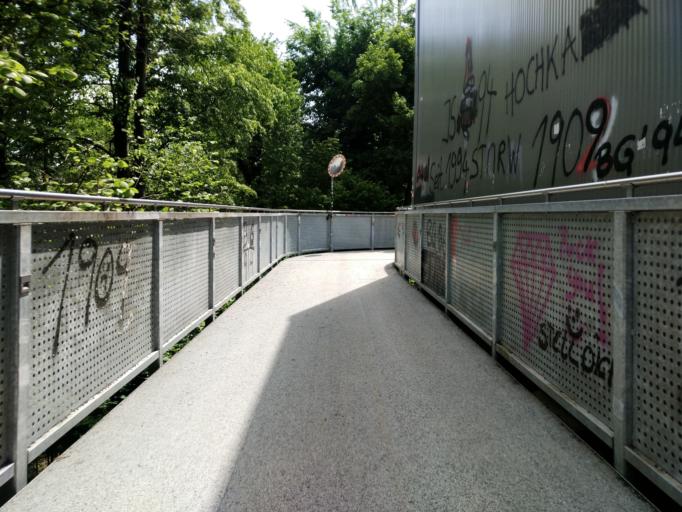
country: AT
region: Styria
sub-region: Graz Stadt
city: Goesting
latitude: 47.1037
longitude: 15.4045
